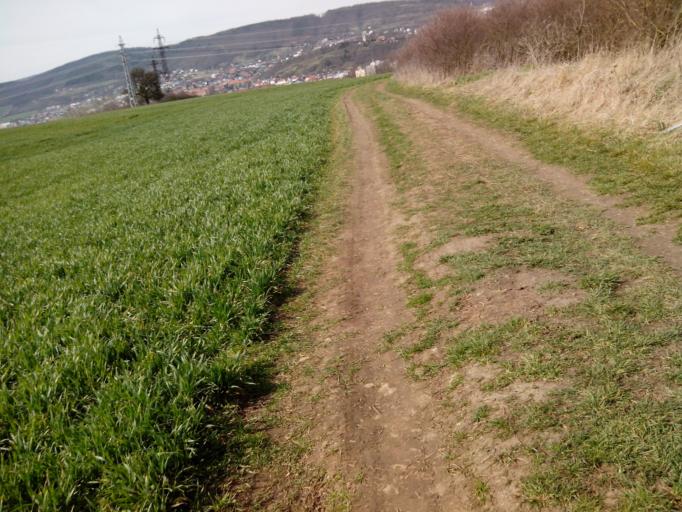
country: CZ
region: Central Bohemia
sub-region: Okres Beroun
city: Beroun
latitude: 49.9520
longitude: 14.0796
